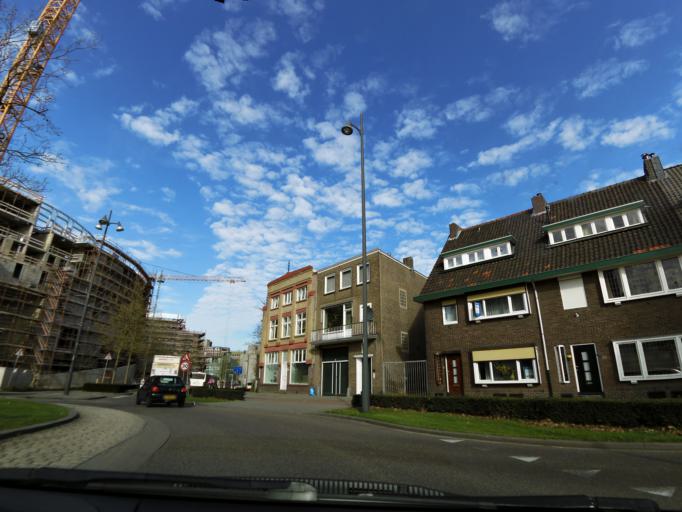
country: NL
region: Limburg
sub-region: Gemeente Heerlen
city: Heerlen
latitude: 50.8920
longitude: 5.9760
